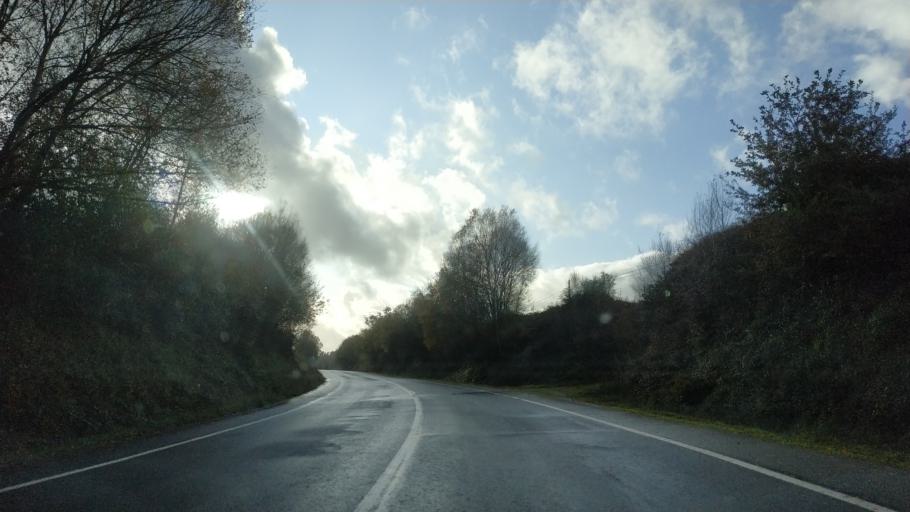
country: ES
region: Galicia
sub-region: Provincia da Coruna
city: Arzua
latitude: 42.9588
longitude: -8.1526
